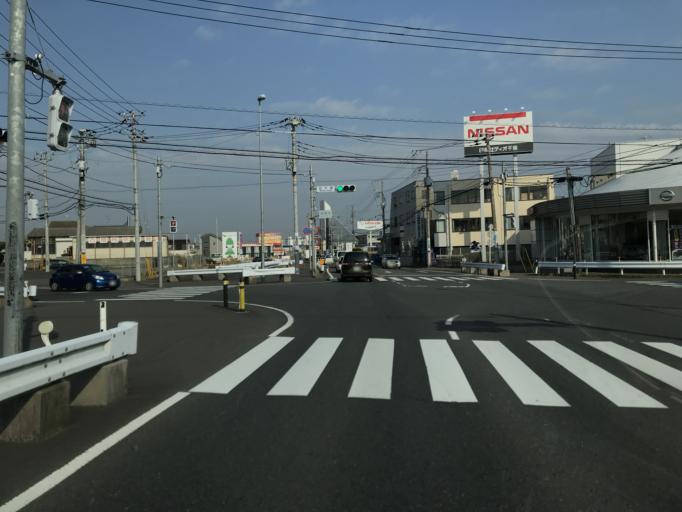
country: JP
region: Chiba
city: Narita
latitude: 35.7507
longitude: 140.3080
